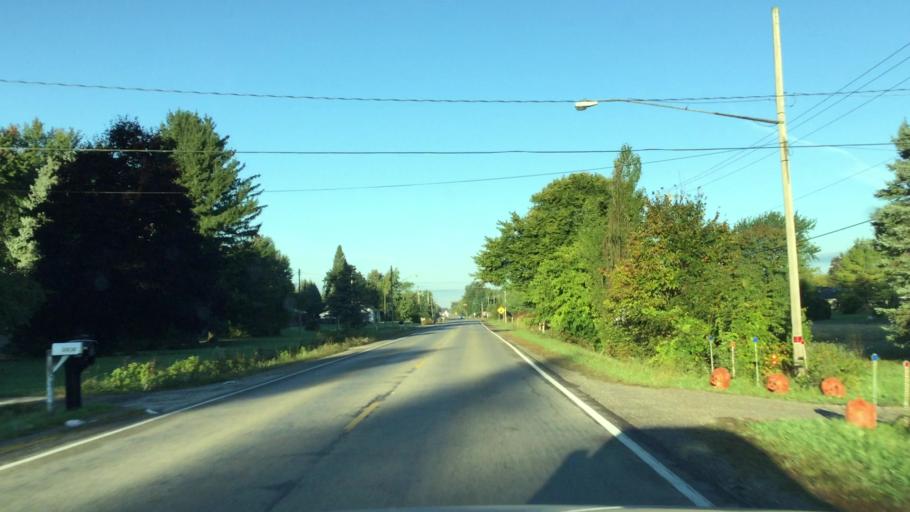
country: US
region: Michigan
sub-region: Genesee County
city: Beecher
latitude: 43.0900
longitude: -83.7491
